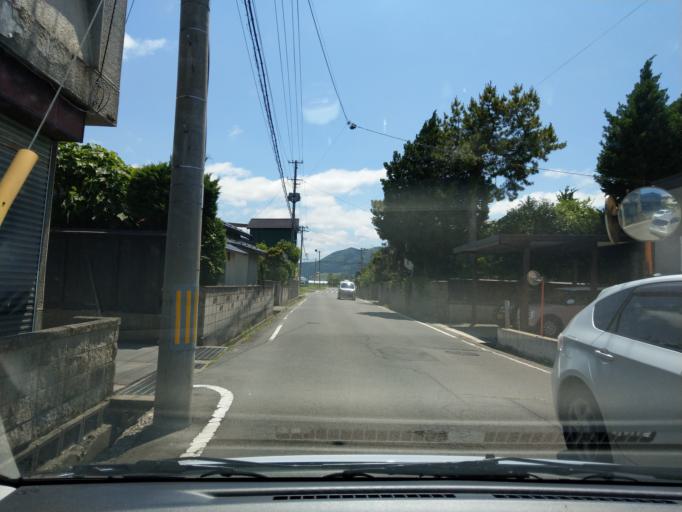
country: JP
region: Aomori
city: Hirosaki
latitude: 40.5663
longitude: 140.5517
